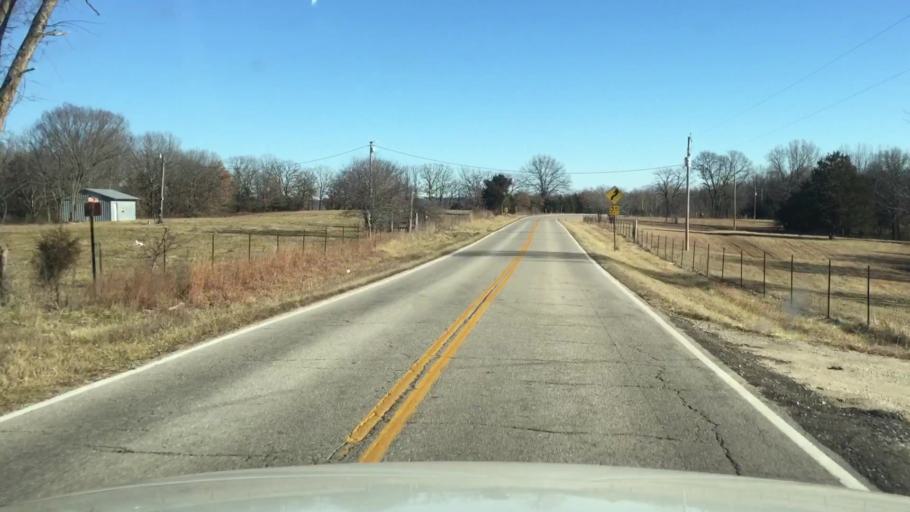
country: US
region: Missouri
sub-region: Morgan County
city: Versailles
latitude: 38.3446
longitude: -92.7350
